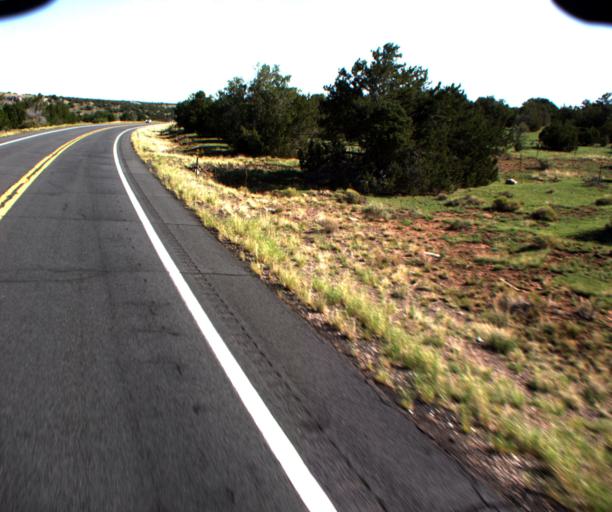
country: US
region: Arizona
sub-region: Coconino County
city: Williams
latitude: 35.4774
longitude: -112.1775
